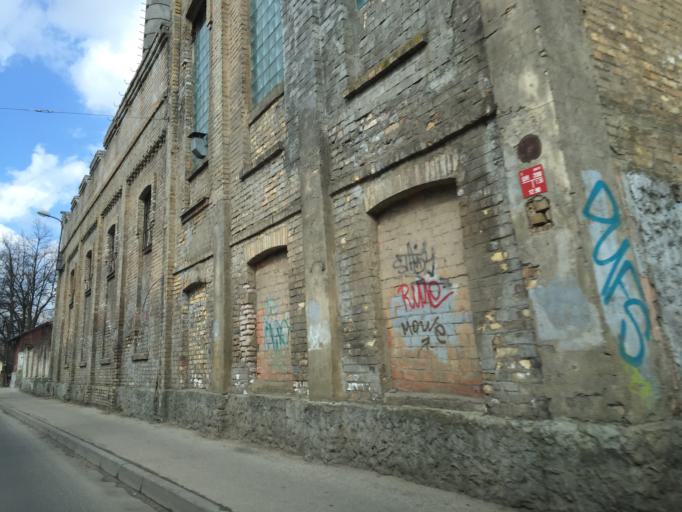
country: LV
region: Riga
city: Riga
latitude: 56.9279
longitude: 24.1656
